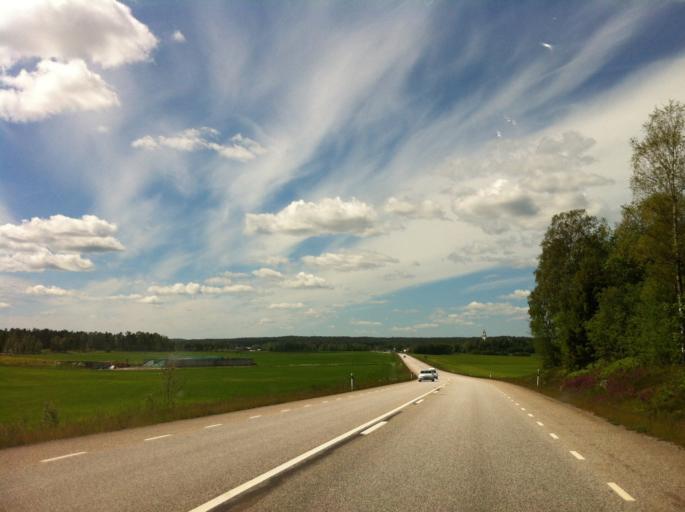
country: SE
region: Vaestra Goetaland
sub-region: Amals Kommun
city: Amal
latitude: 58.9840
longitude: 12.6577
